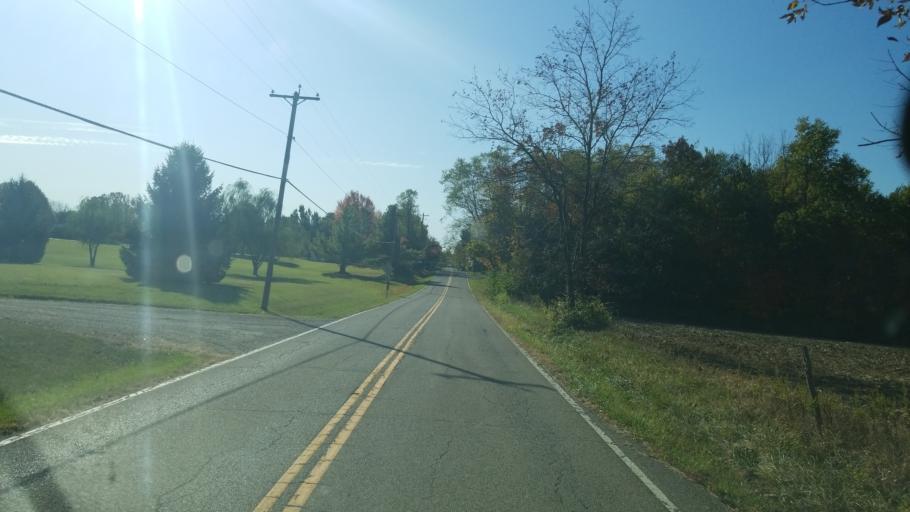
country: US
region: Ohio
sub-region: Warren County
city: Morrow
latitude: 39.4172
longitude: -84.0805
